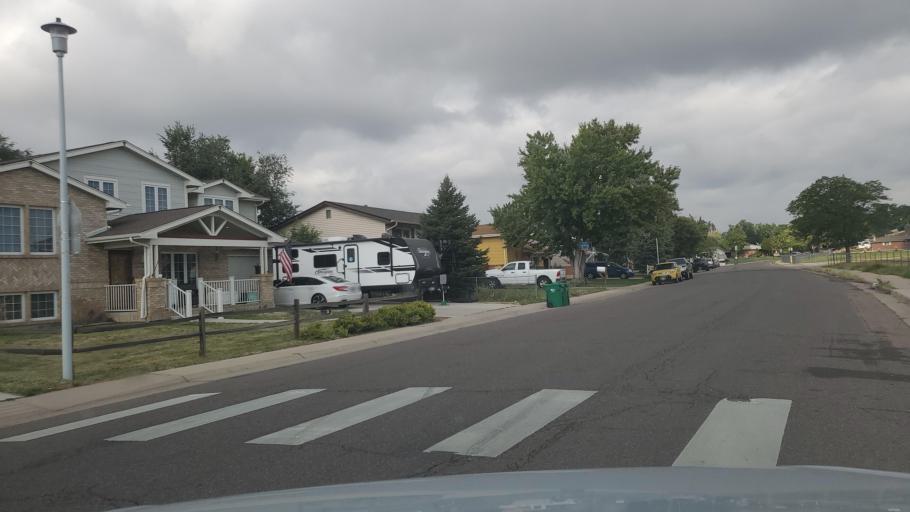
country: US
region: Colorado
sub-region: Adams County
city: Welby
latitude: 39.8465
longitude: -104.9691
